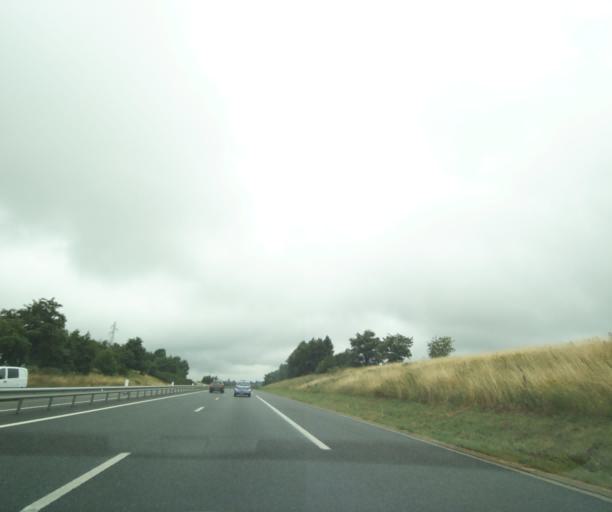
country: FR
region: Midi-Pyrenees
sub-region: Departement de l'Aveyron
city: Luc-la-Primaube
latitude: 44.2969
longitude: 2.5229
